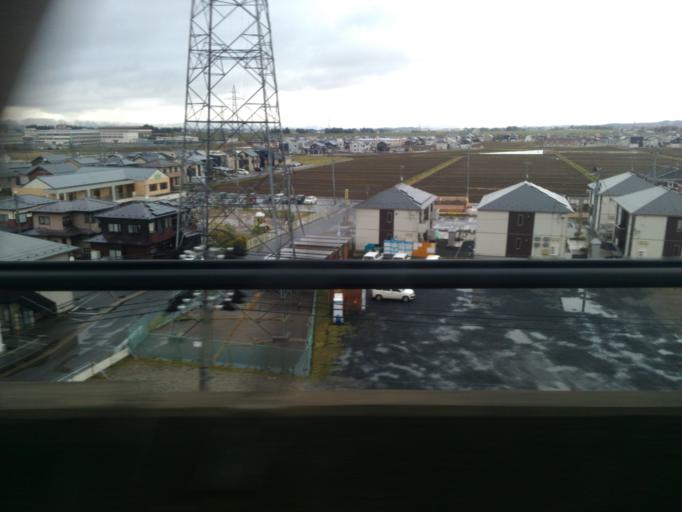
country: JP
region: Miyagi
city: Furukawa
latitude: 38.5632
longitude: 140.9657
